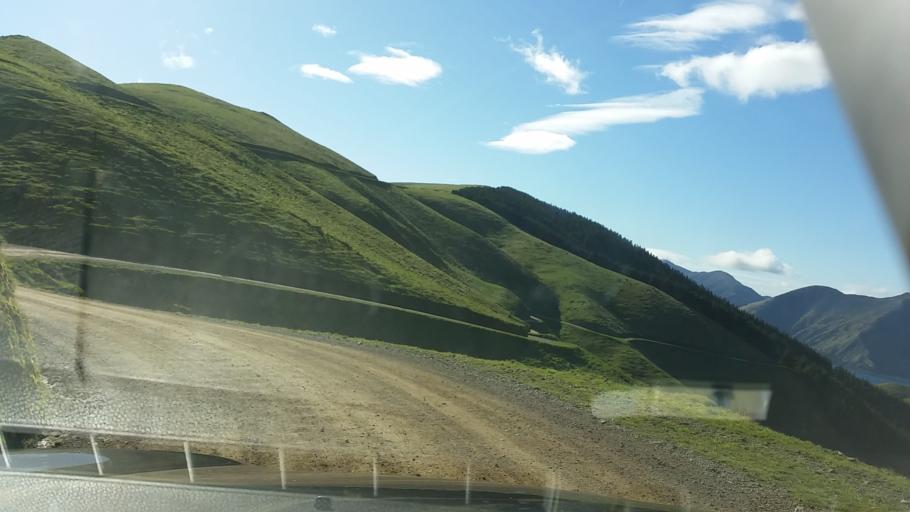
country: NZ
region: Marlborough
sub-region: Marlborough District
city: Picton
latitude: -40.9893
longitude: 173.8056
